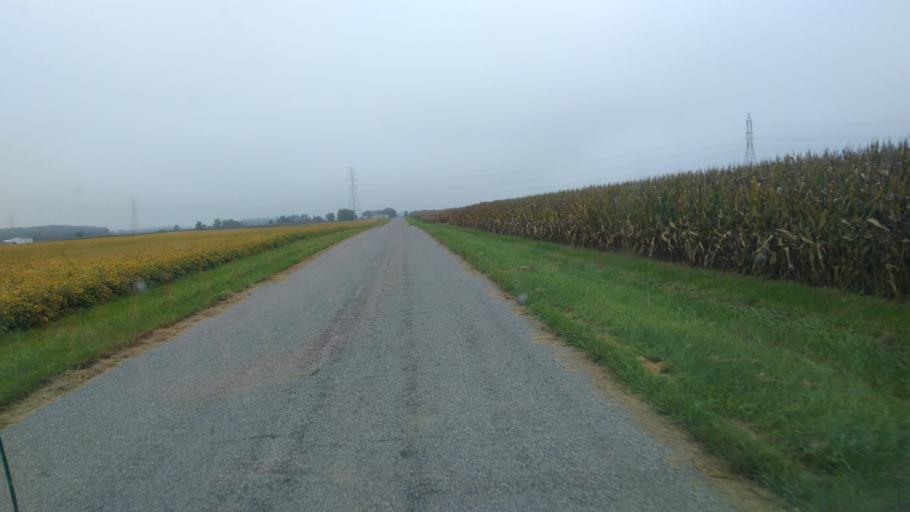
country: US
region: Ohio
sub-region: Logan County
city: Northwood
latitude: 40.4978
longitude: -83.5973
